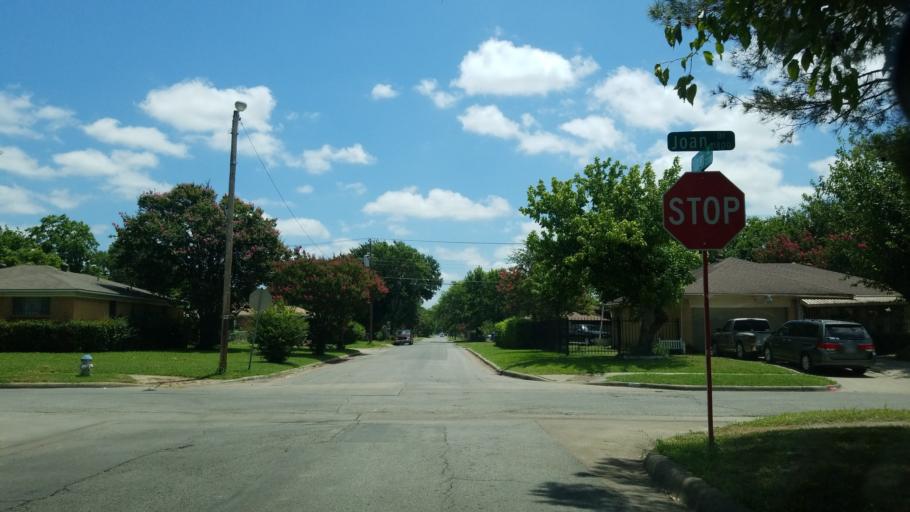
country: US
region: Texas
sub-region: Dallas County
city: Balch Springs
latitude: 32.7445
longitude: -96.6975
